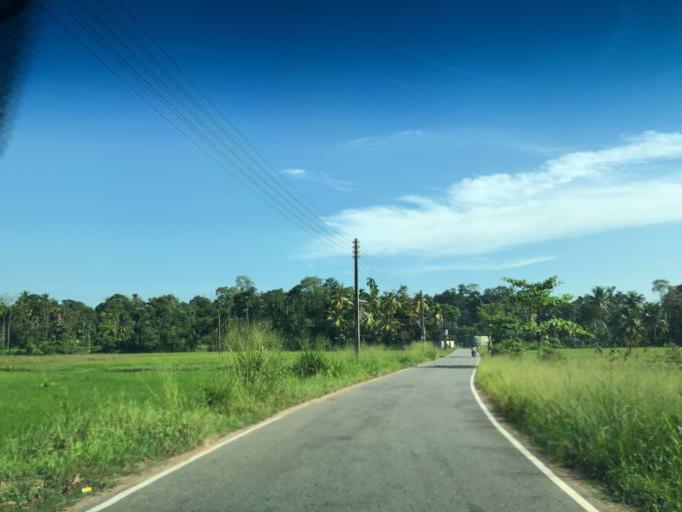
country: LK
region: Western
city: Homagama
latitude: 6.7955
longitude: 79.9793
